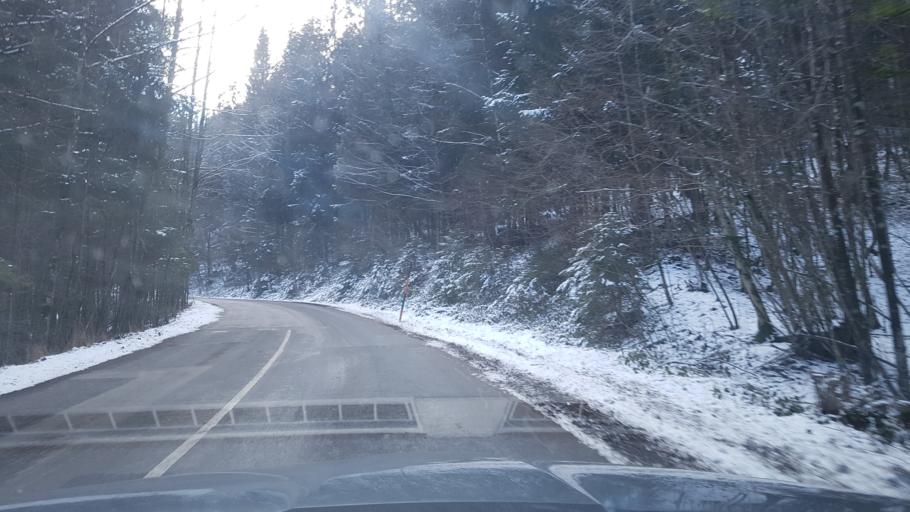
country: AT
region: Salzburg
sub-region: Politischer Bezirk Hallein
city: Kuchl
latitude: 47.6178
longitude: 13.1347
